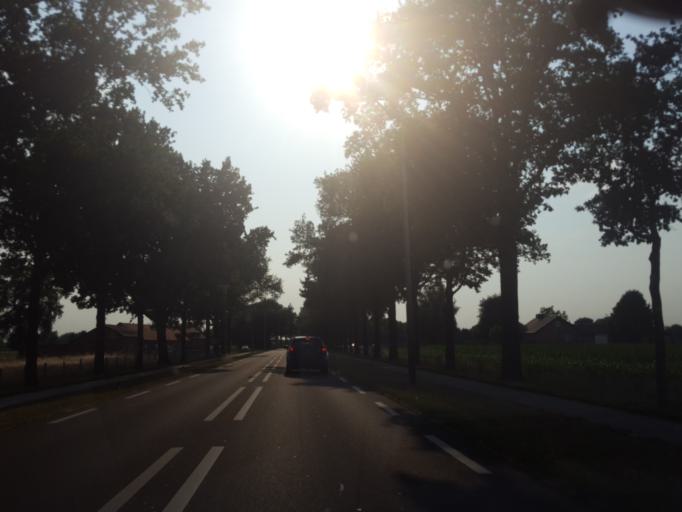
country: NL
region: Limburg
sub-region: Gemeente Leudal
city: Kelpen-Oler
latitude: 51.2356
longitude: 5.7881
